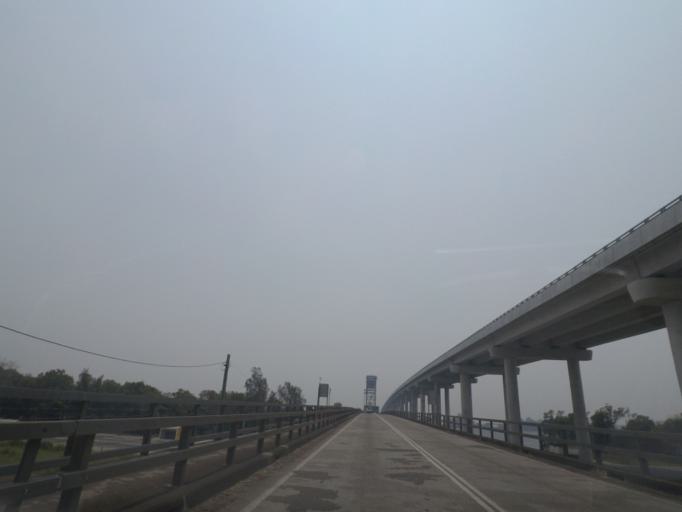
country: AU
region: New South Wales
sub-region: Clarence Valley
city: Maclean
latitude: -29.4335
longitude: 153.2407
